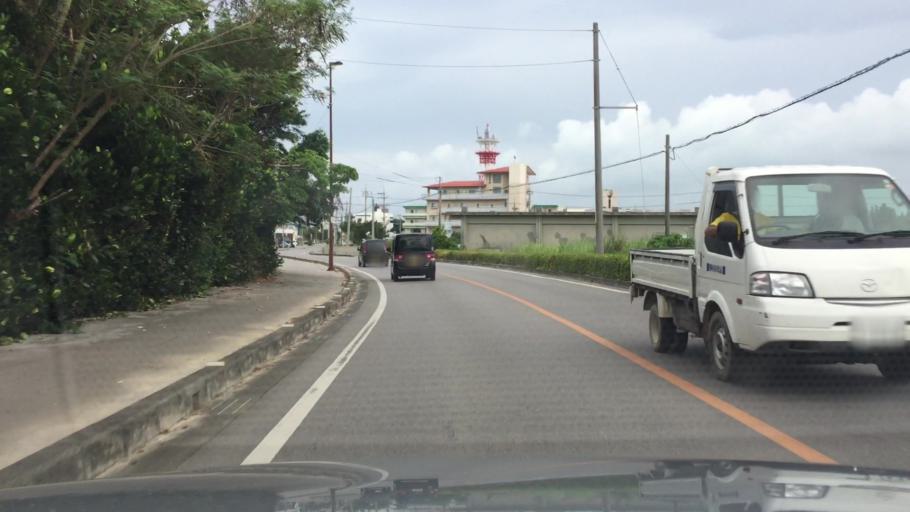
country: JP
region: Okinawa
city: Ishigaki
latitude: 24.3533
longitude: 124.1578
